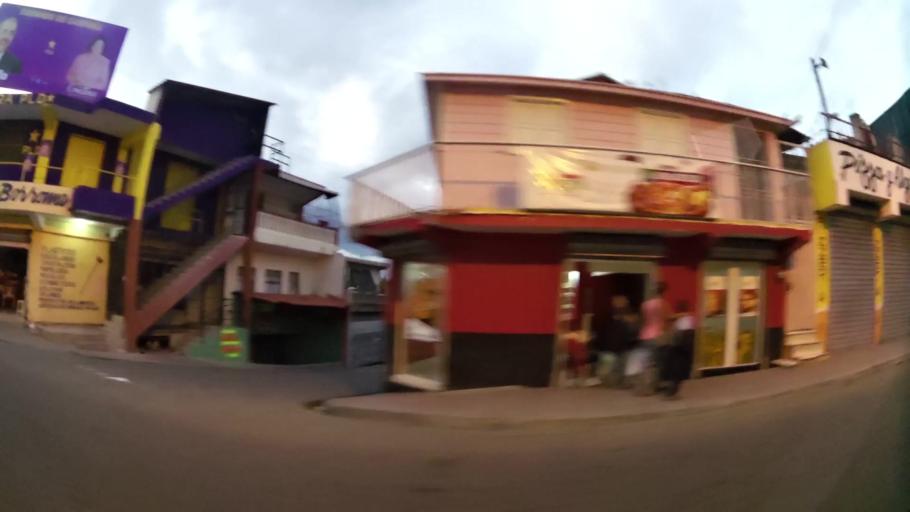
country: DO
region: Santo Domingo
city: Santo Domingo Oeste
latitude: 18.5252
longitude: -70.0257
